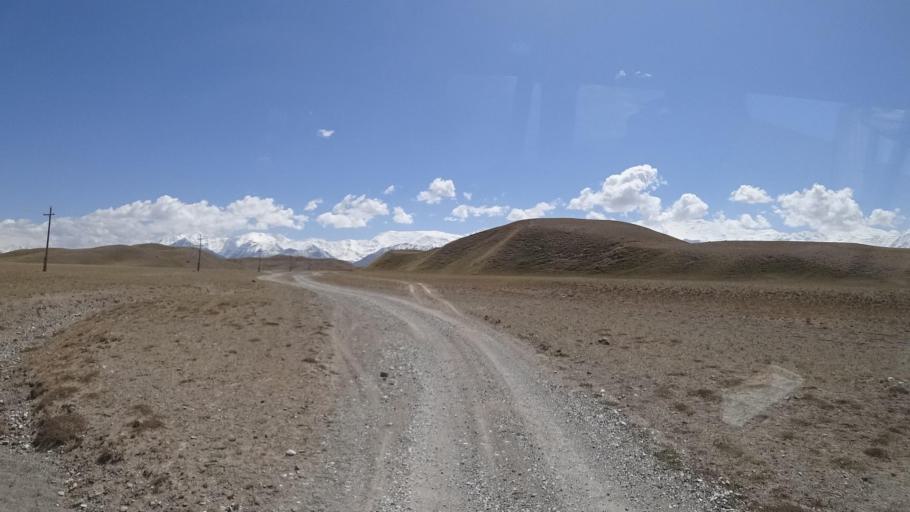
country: KG
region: Osh
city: Gul'cha
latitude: 39.6077
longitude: 72.8765
